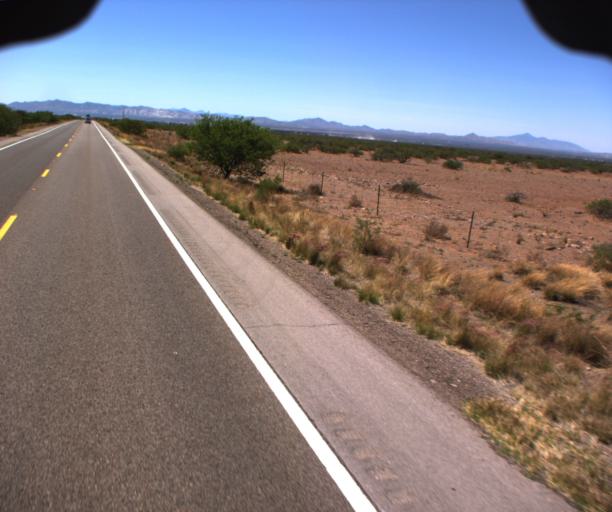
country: US
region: Arizona
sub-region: Cochise County
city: Douglas
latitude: 31.4068
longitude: -109.5002
